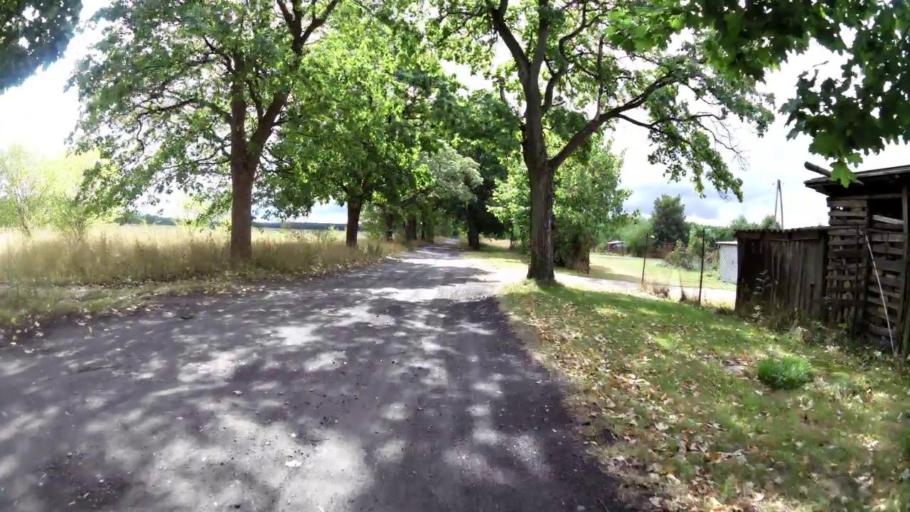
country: PL
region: West Pomeranian Voivodeship
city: Trzcinsko Zdroj
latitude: 52.8803
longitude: 14.7111
